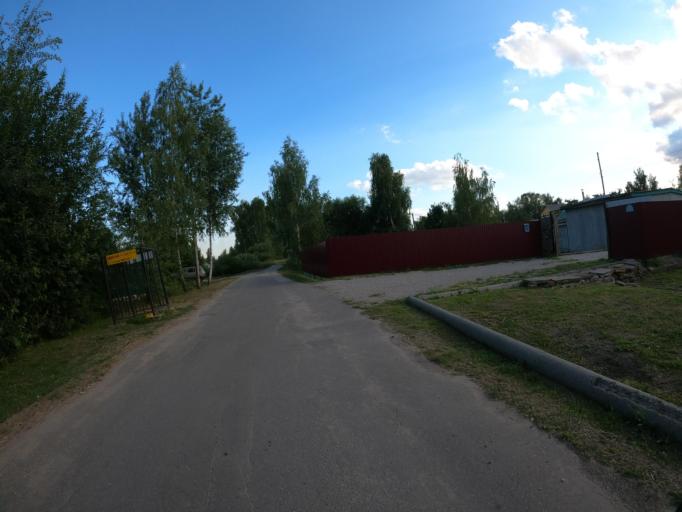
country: RU
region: Moskovskaya
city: Ashitkovo
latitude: 55.4236
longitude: 38.5821
